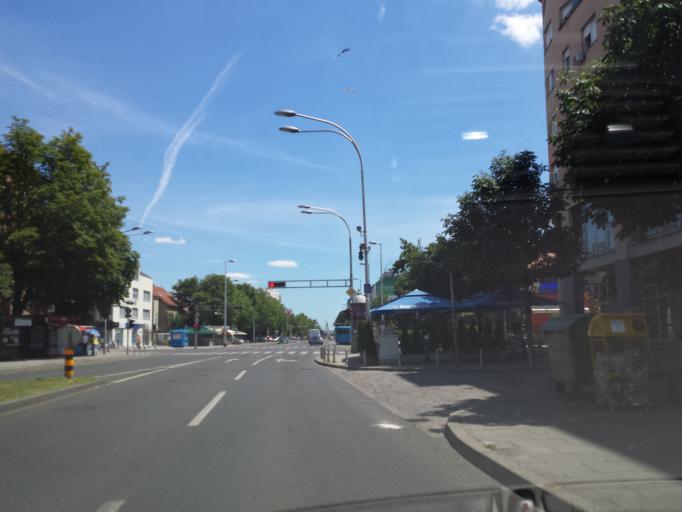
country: HR
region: Grad Zagreb
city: Zagreb
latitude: 45.8137
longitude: 15.9980
